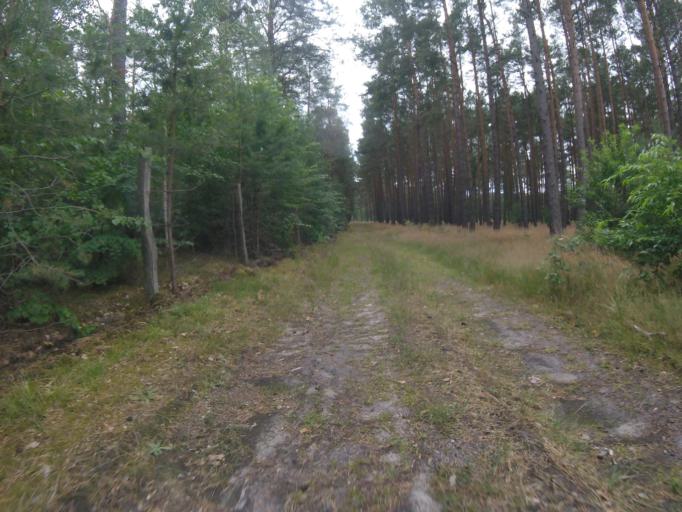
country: DE
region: Brandenburg
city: Bestensee
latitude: 52.2726
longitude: 13.7143
